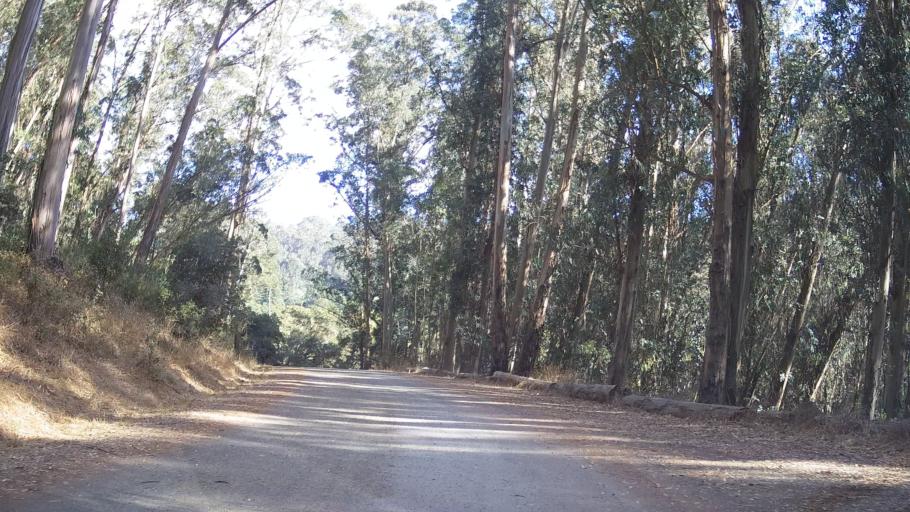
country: US
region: California
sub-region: Contra Costa County
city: Kensington
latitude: 37.9073
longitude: -122.2621
